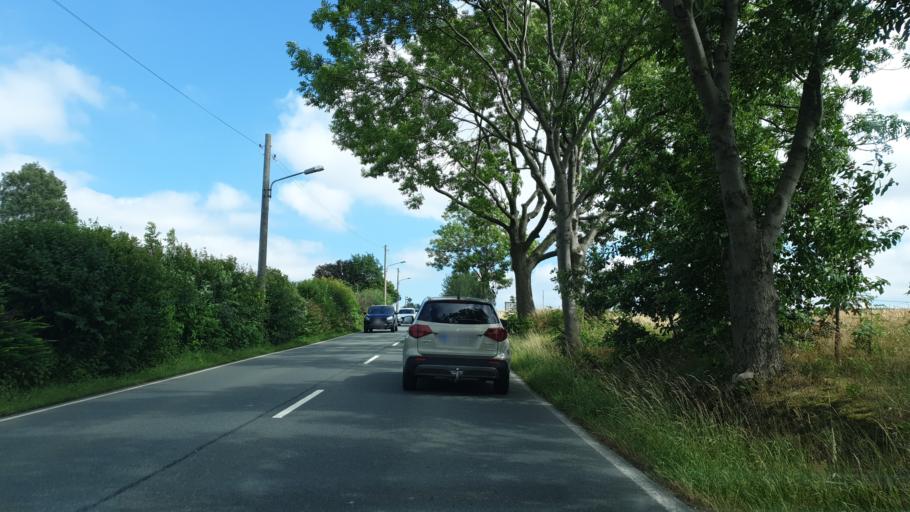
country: DE
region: Saxony
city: Neukirchen
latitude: 50.7940
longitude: 12.8670
